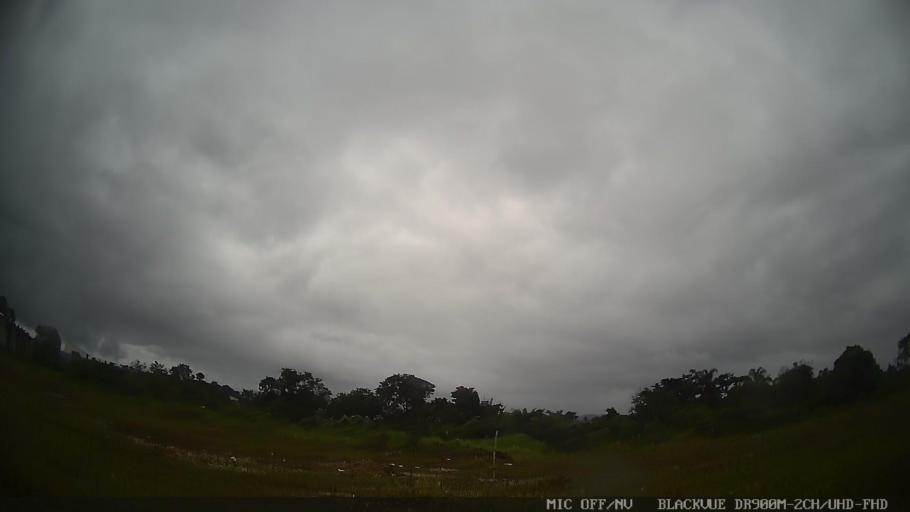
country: BR
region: Sao Paulo
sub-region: Itanhaem
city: Itanhaem
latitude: -24.1851
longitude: -46.8292
